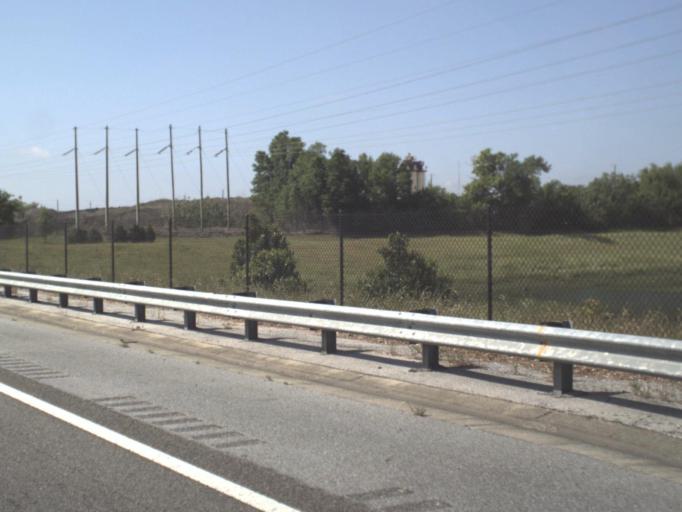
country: US
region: Florida
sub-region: Escambia County
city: Brent
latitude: 30.4585
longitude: -87.2248
